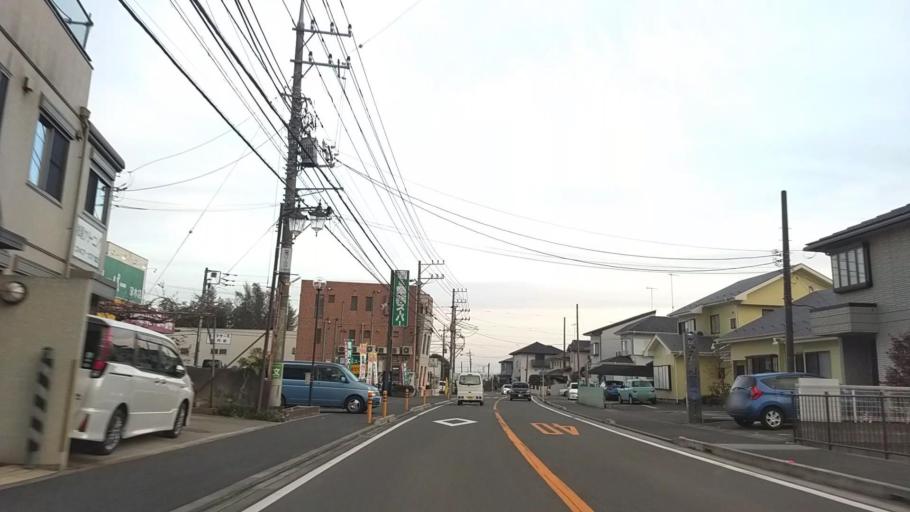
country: JP
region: Kanagawa
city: Atsugi
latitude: 35.4335
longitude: 139.3251
